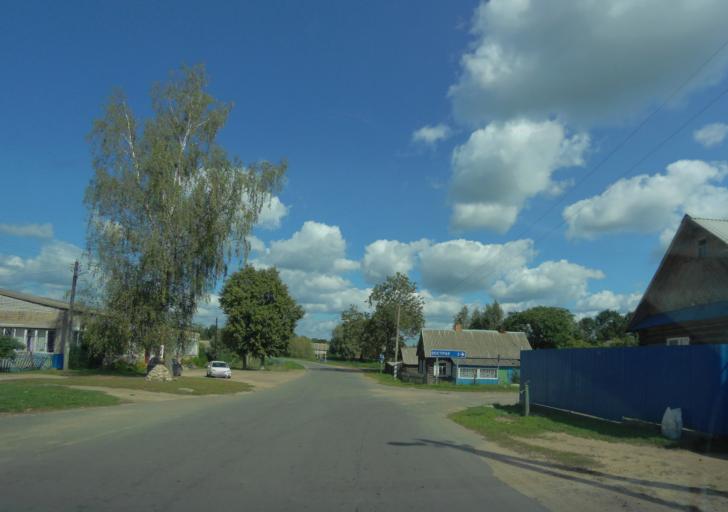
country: BY
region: Minsk
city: Horad Barysaw
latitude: 54.4295
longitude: 28.4313
